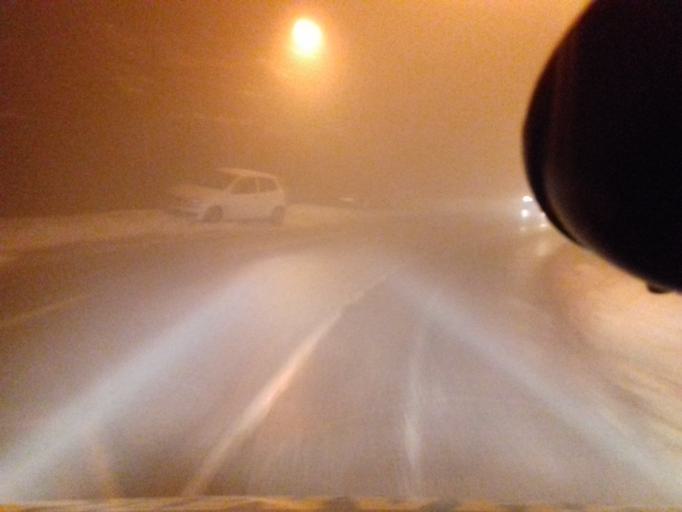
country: BA
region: Federation of Bosnia and Herzegovina
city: Kobilja Glava
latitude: 43.8660
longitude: 18.4158
